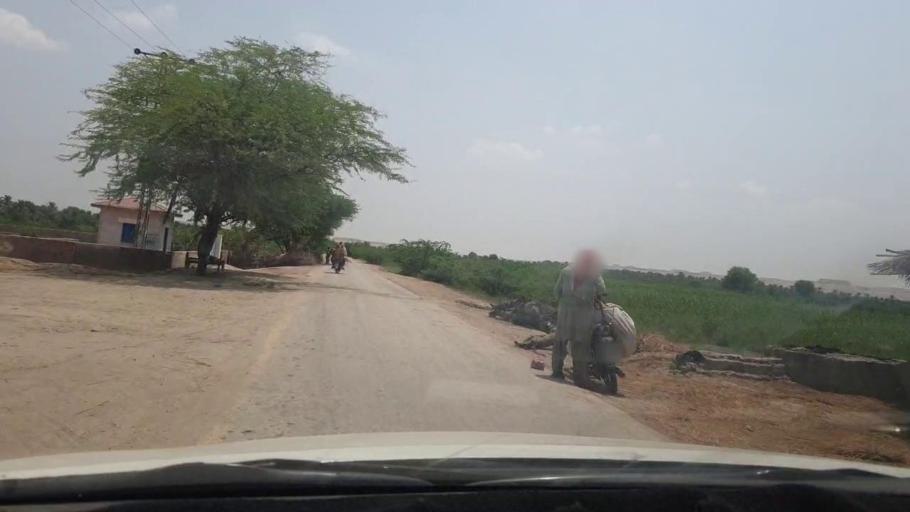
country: PK
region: Sindh
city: Khairpur
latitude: 27.5352
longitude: 68.8872
